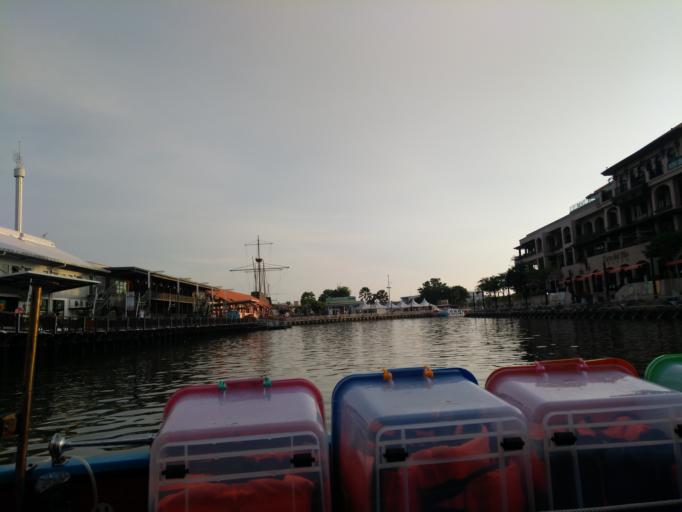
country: MY
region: Melaka
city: Malacca
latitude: 2.1939
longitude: 102.2476
